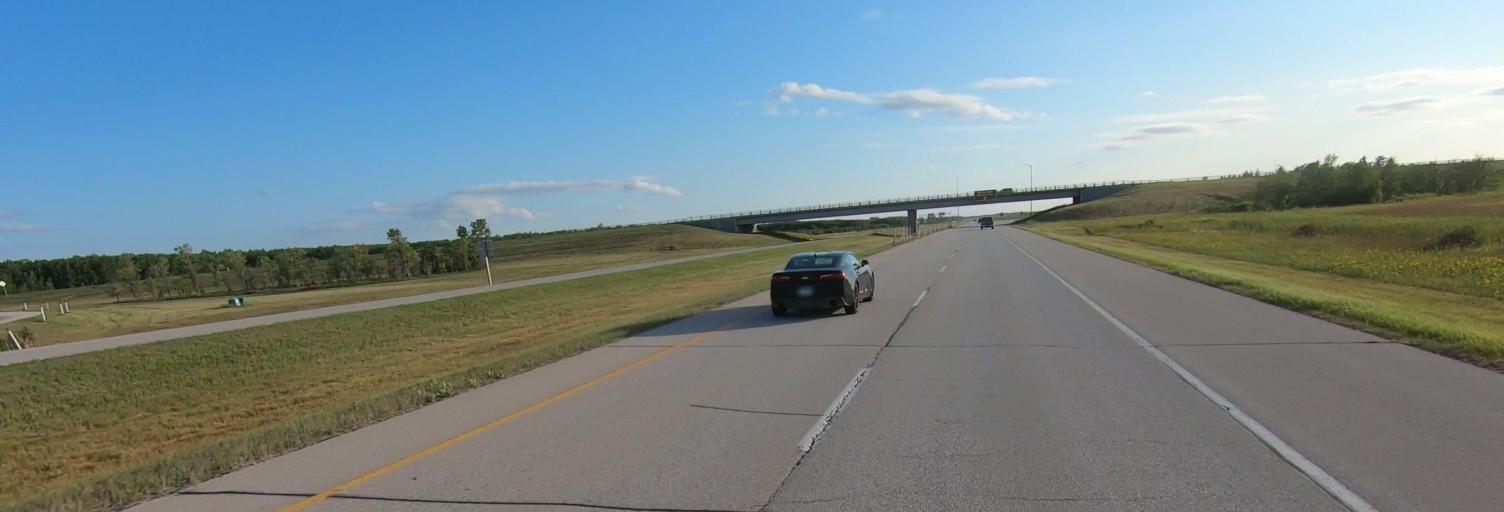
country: CA
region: Manitoba
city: Selkirk
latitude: 50.0212
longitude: -96.9399
